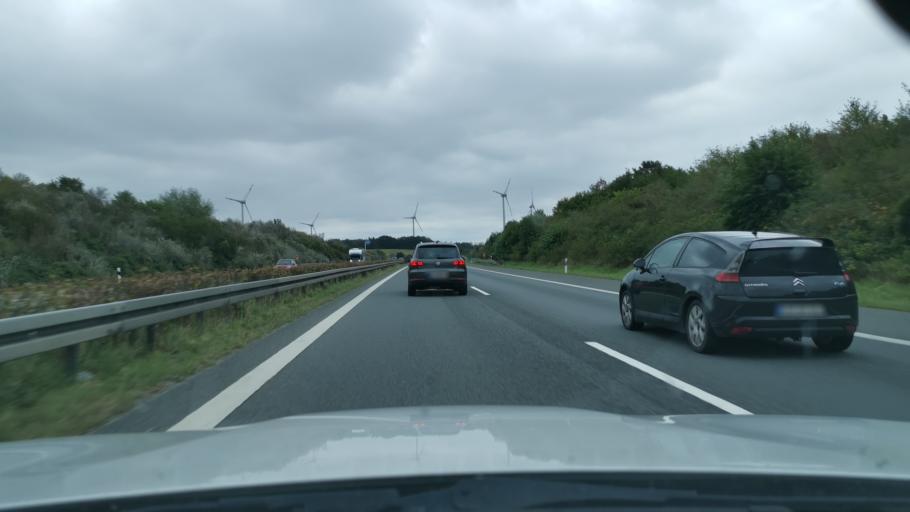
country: DE
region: Mecklenburg-Vorpommern
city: Laage
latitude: 53.8406
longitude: 12.2886
